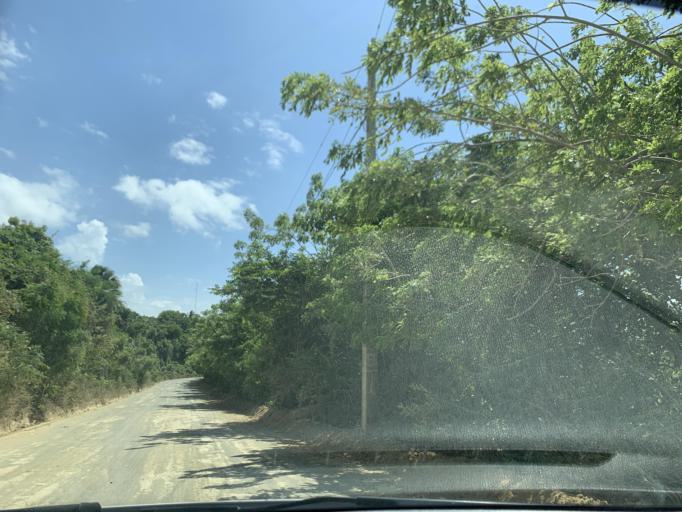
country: DO
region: Puerto Plata
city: Luperon
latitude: 19.8838
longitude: -70.8329
